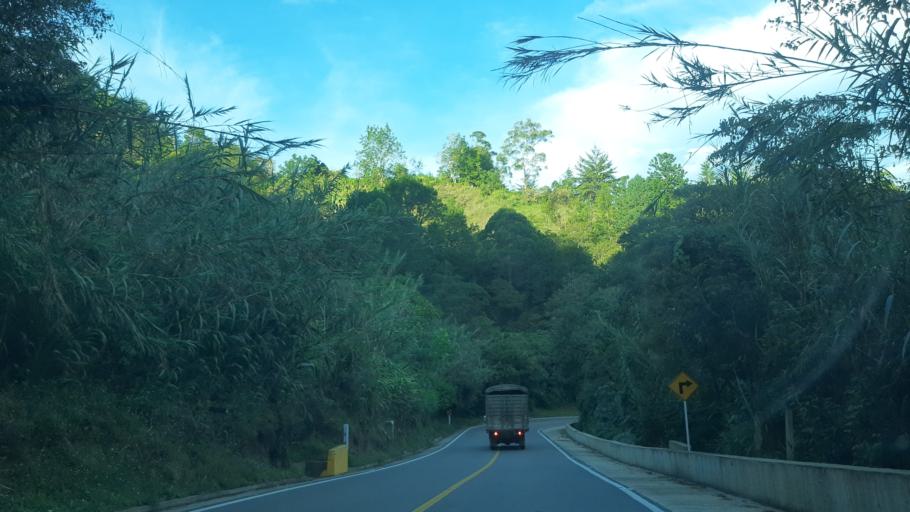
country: CO
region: Boyaca
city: Guateque
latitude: 5.0069
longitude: -73.4966
